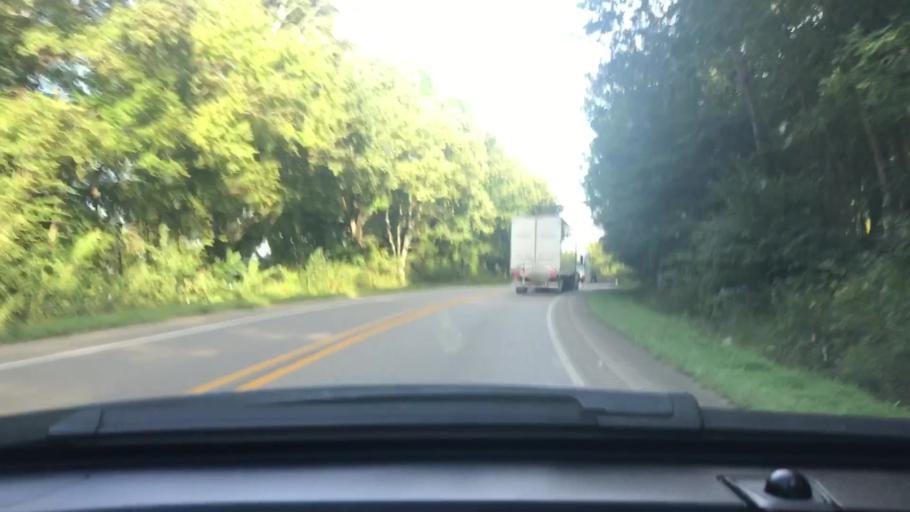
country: US
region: Arkansas
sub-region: Randolph County
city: Pocahontas
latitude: 36.2128
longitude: -91.2063
